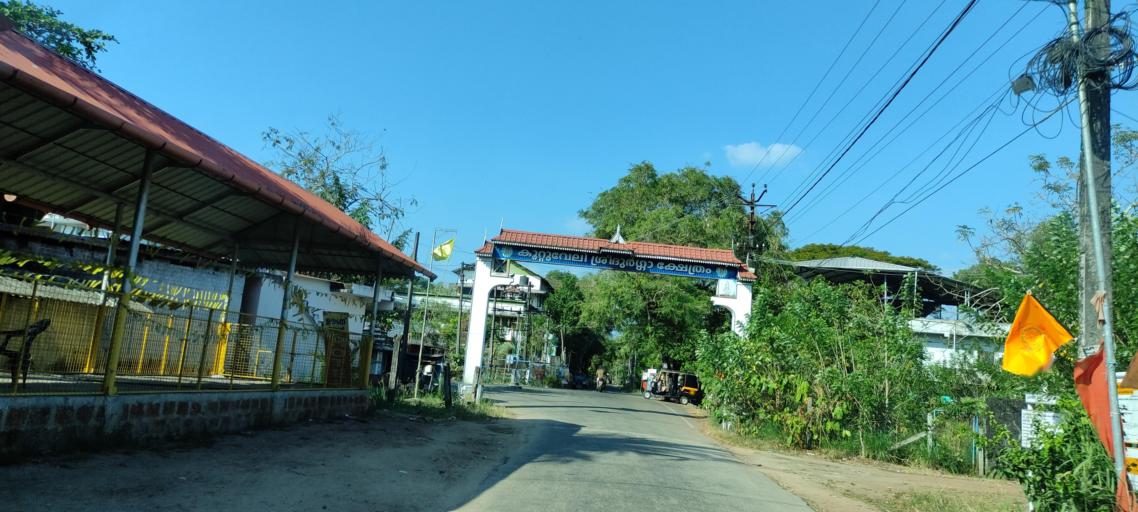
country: IN
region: Kerala
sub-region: Alappuzha
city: Shertallai
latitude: 9.6380
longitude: 76.3437
